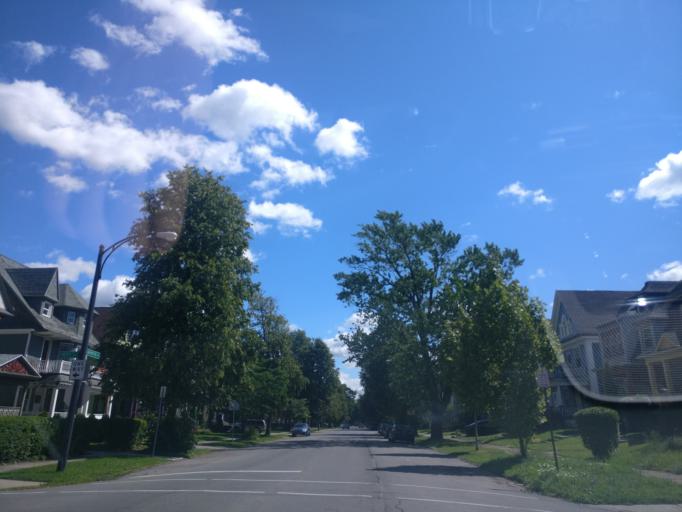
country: US
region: New York
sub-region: Erie County
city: Buffalo
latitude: 42.9202
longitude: -78.8868
